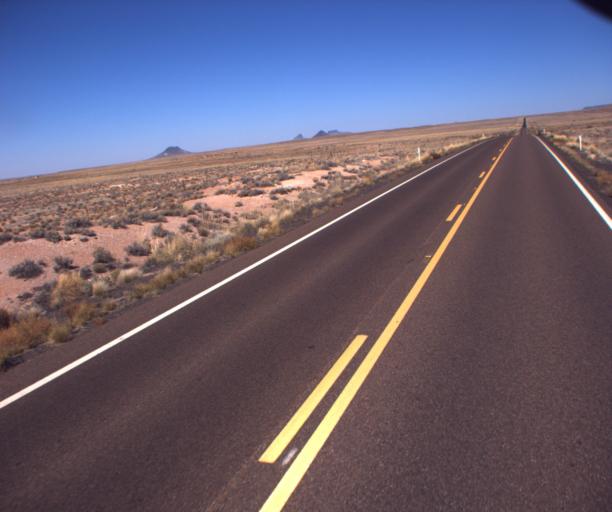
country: US
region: Arizona
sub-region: Navajo County
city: Dilkon
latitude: 35.2524
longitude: -110.4299
